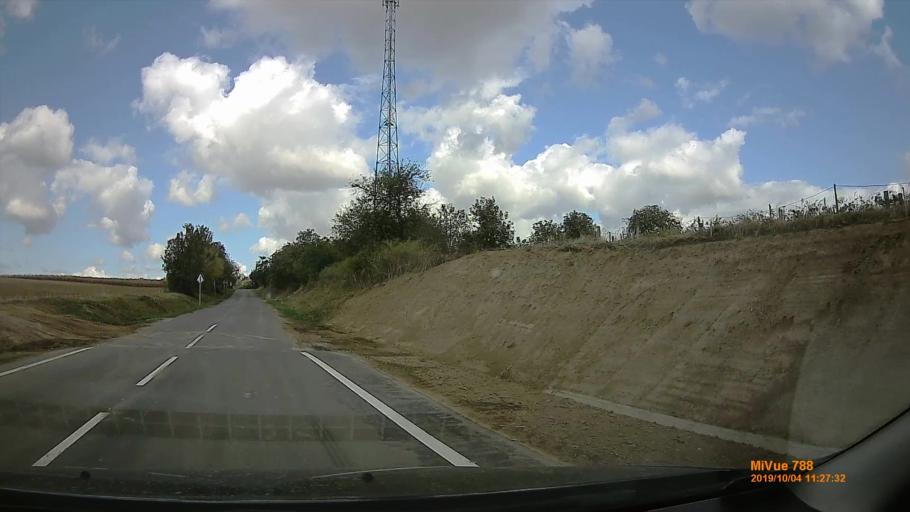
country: HU
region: Somogy
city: Kaposvar
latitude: 46.5158
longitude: 17.8084
